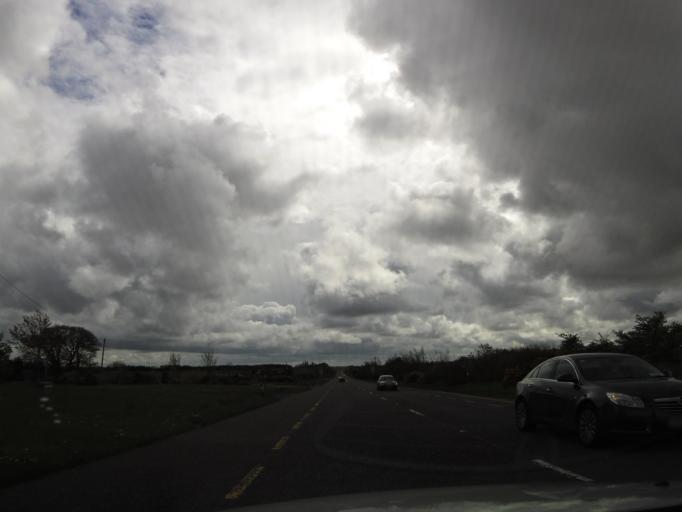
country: IE
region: Connaught
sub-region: Maigh Eo
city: Claremorris
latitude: 53.7549
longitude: -8.9648
